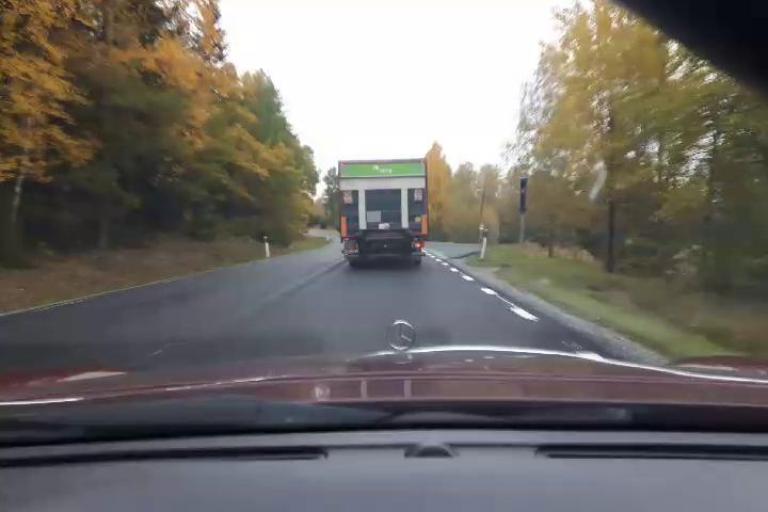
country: SE
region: Soedermanland
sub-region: Strangnas Kommun
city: Strangnas
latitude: 59.4297
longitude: 17.0250
